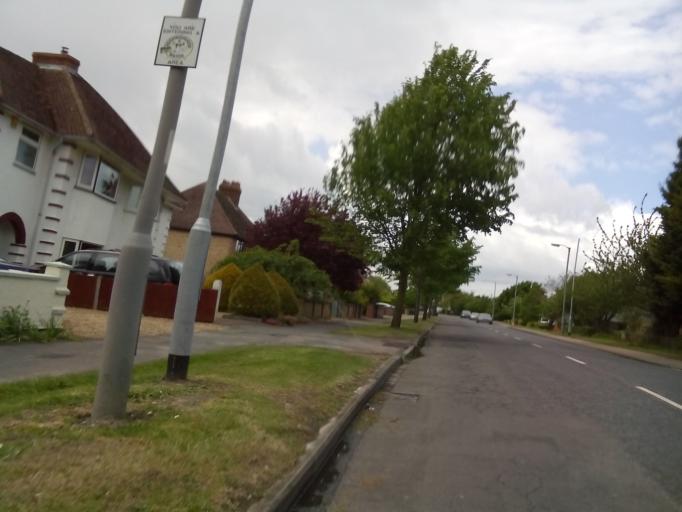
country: GB
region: England
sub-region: Cambridgeshire
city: Fulbourn
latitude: 52.1929
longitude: 0.1756
